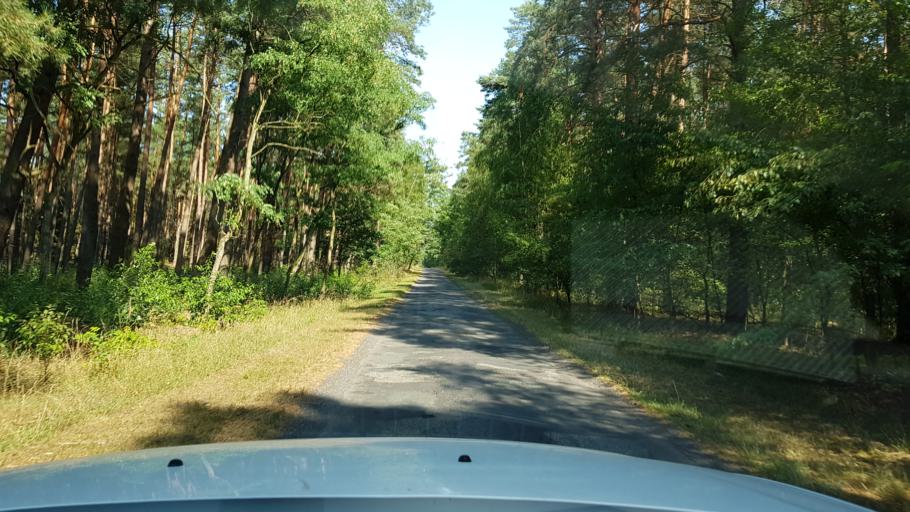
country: PL
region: West Pomeranian Voivodeship
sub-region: Powiat gryfinski
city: Moryn
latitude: 52.8212
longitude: 14.3533
